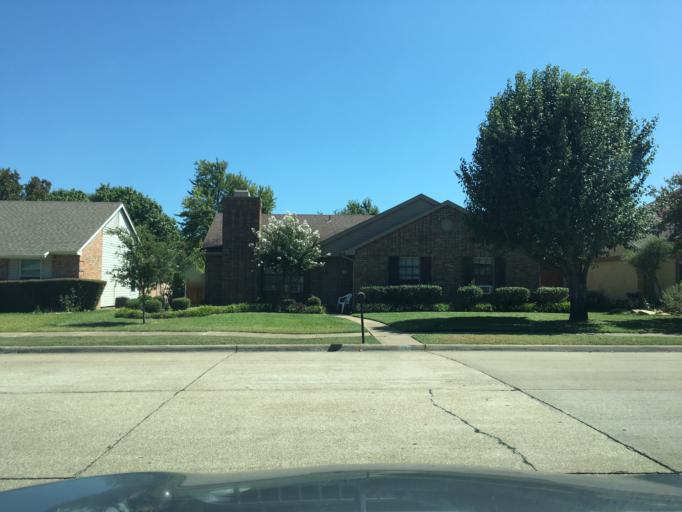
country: US
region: Texas
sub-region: Dallas County
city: Garland
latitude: 32.9512
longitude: -96.6288
